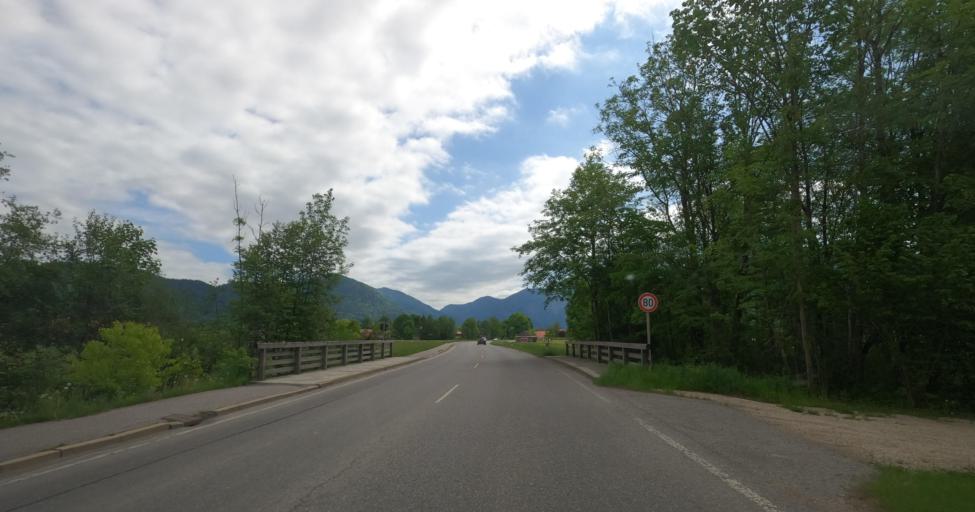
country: DE
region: Bavaria
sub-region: Upper Bavaria
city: Tegernsee
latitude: 47.6914
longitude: 11.7405
